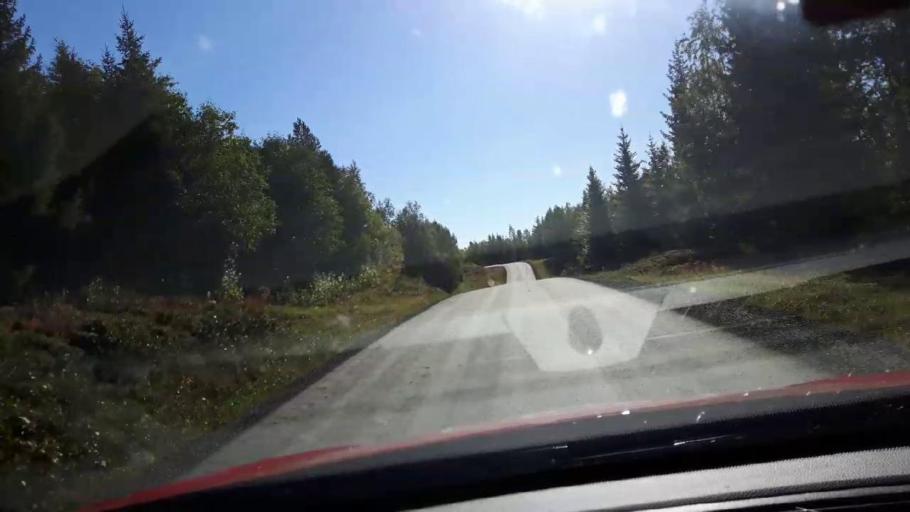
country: NO
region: Nord-Trondelag
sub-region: Lierne
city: Sandvika
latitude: 64.5996
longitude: 13.9732
